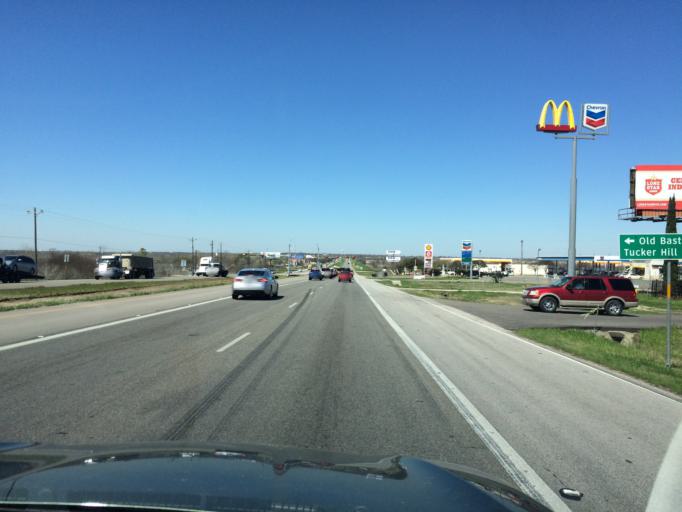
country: US
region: Texas
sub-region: Travis County
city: Garfield
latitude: 30.1742
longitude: -97.5251
